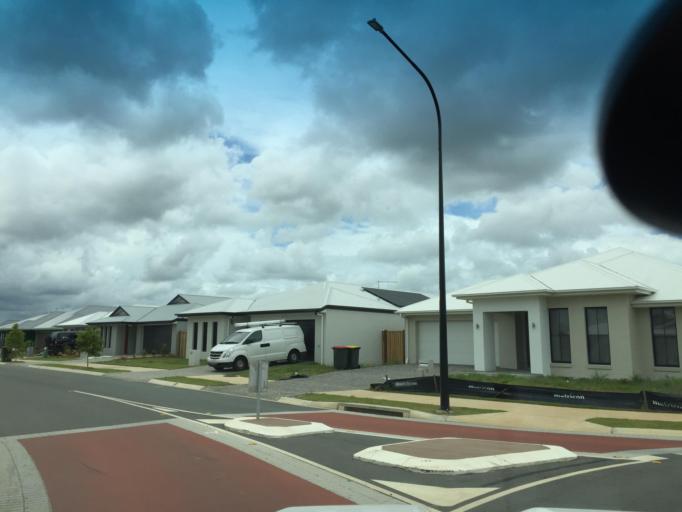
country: AU
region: Queensland
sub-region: Moreton Bay
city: Caboolture
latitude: -27.0641
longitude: 152.9242
